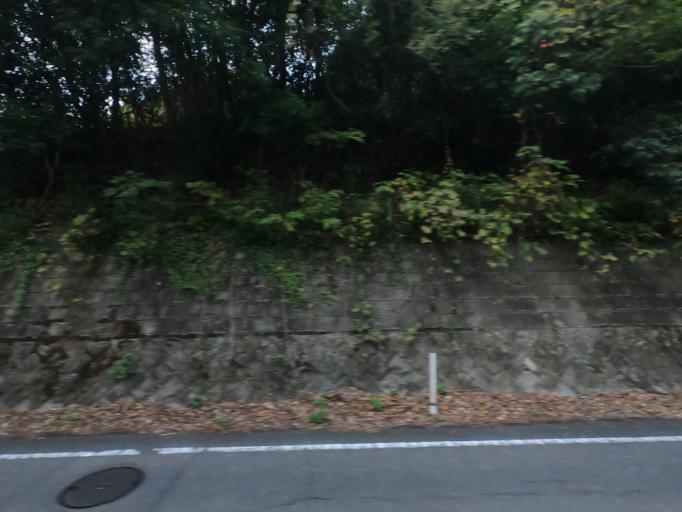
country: JP
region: Kumamoto
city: Minamata
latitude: 32.2458
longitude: 130.4756
